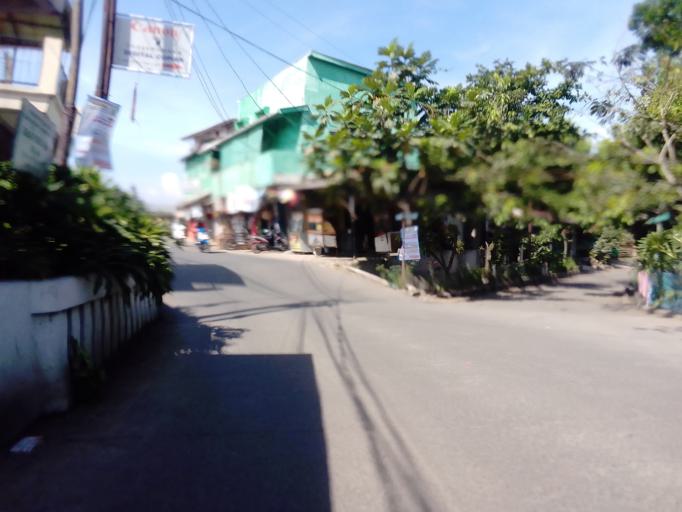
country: ID
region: West Java
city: Bandung
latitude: -6.9456
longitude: 107.6702
